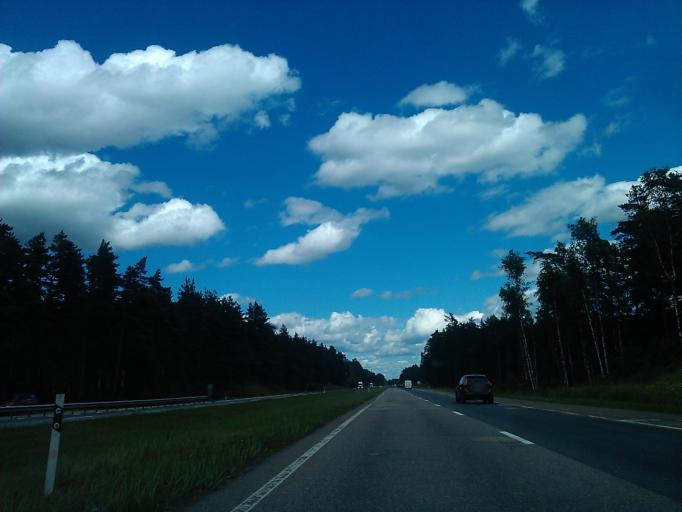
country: LV
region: Garkalne
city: Garkalne
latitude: 57.0311
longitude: 24.3737
